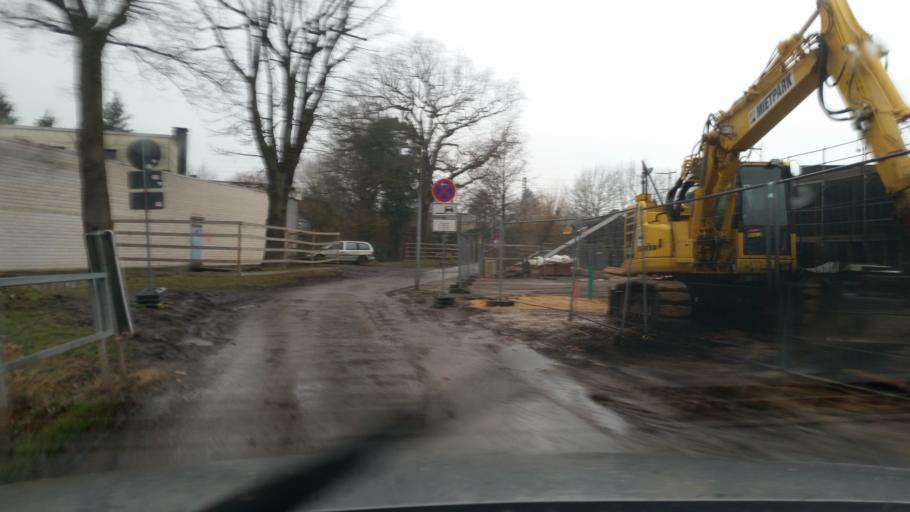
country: DE
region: Lower Saxony
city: Langenhagen
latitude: 52.4639
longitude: 9.7414
